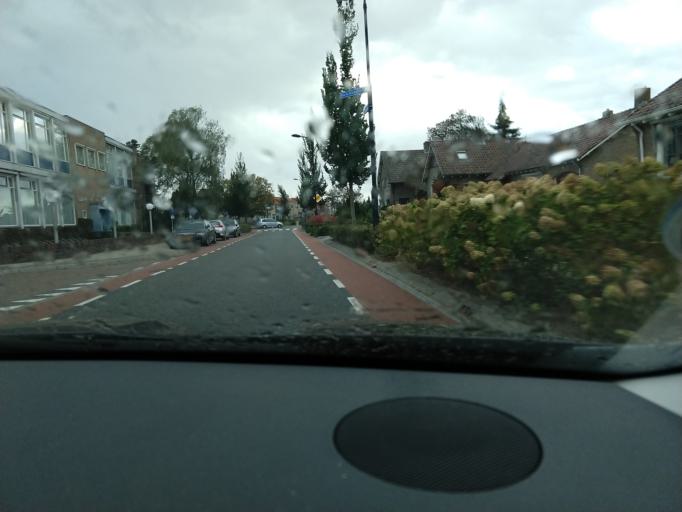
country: NL
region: Zeeland
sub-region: Gemeente Reimerswaal
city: Yerseke
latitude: 51.4944
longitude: 4.0455
